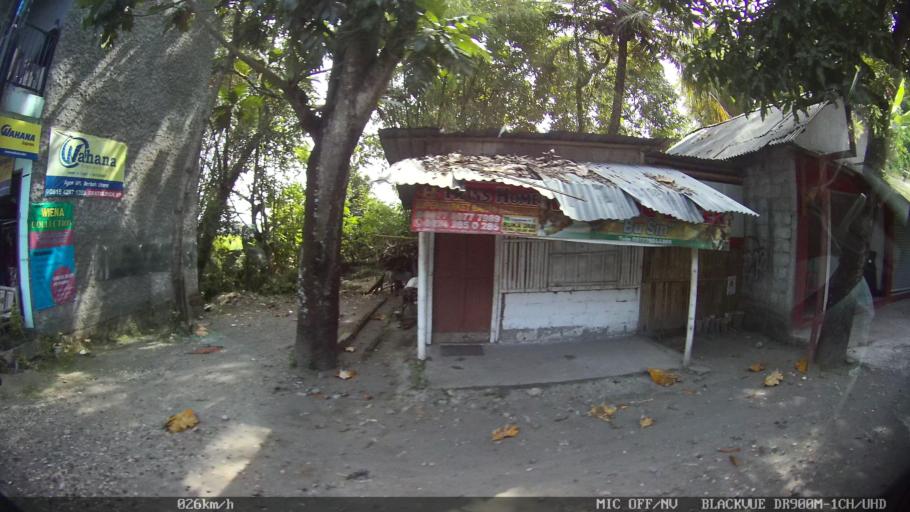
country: ID
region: Daerah Istimewa Yogyakarta
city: Depok
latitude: -7.8002
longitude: 110.4453
